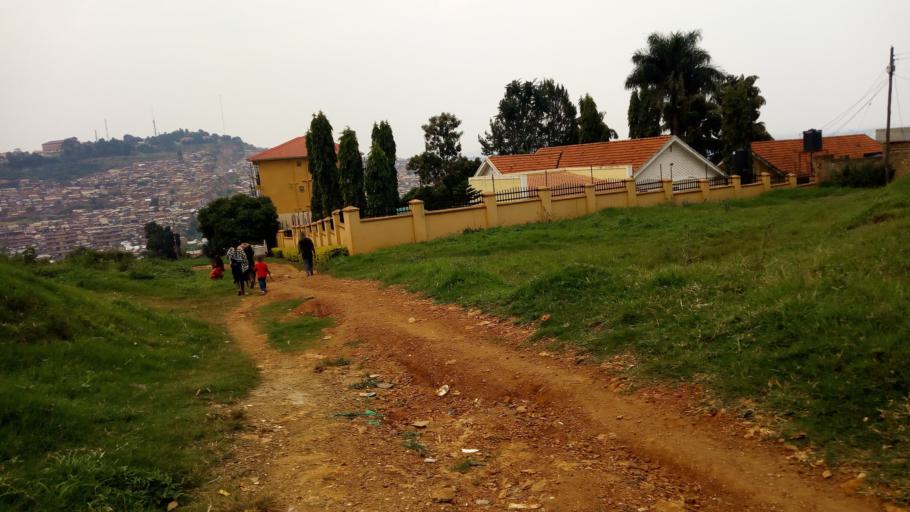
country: UG
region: Central Region
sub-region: Wakiso District
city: Kireka
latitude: 0.3287
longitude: 32.6348
